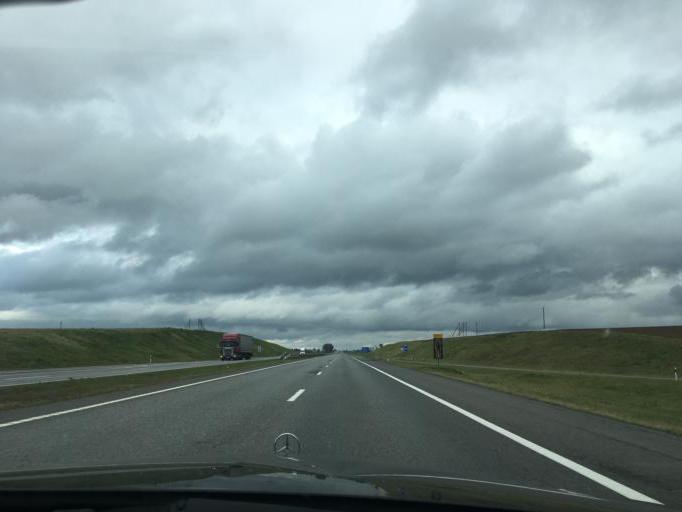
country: BY
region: Vitebsk
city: Kokhanava
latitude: 54.4769
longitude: 29.9180
